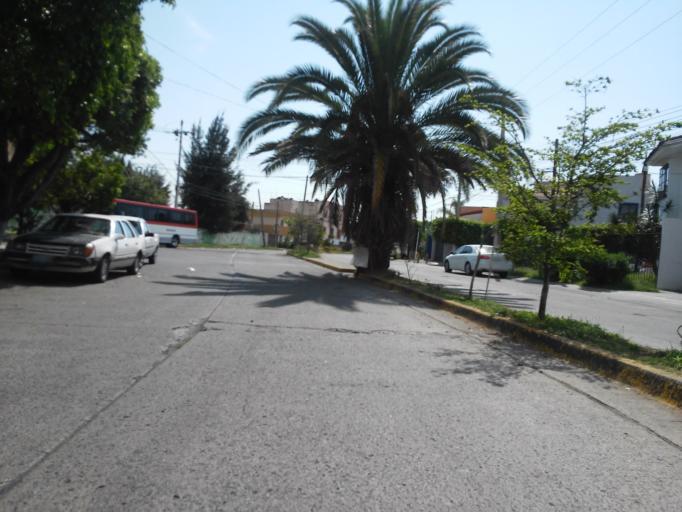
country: MX
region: Jalisco
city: Guadalajara
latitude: 20.6542
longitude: -103.4189
